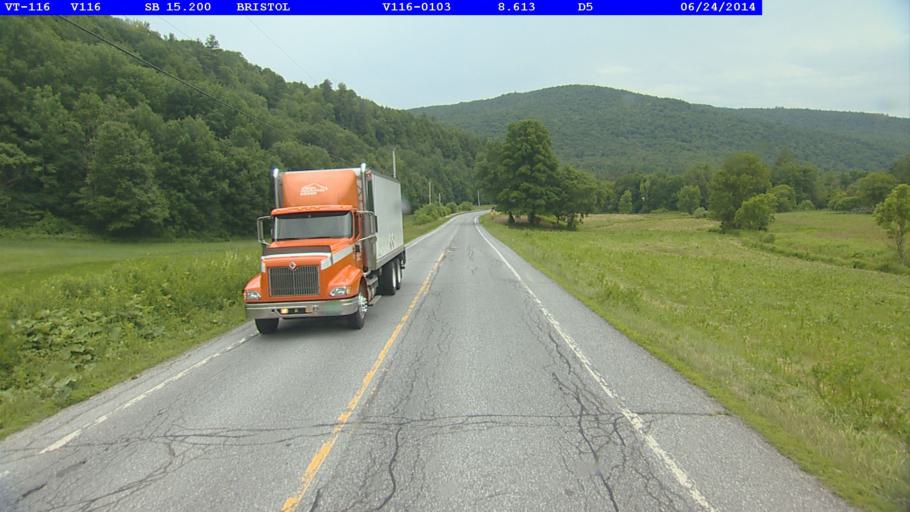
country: US
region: Vermont
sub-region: Addison County
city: Bristol
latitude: 44.1347
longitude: -73.0459
